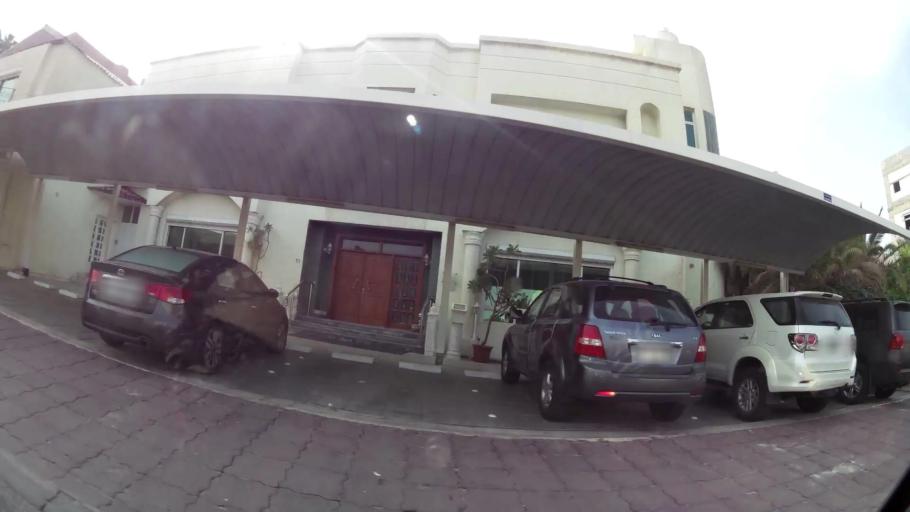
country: KW
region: Al Asimah
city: Ash Shamiyah
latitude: 29.3130
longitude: 47.9688
